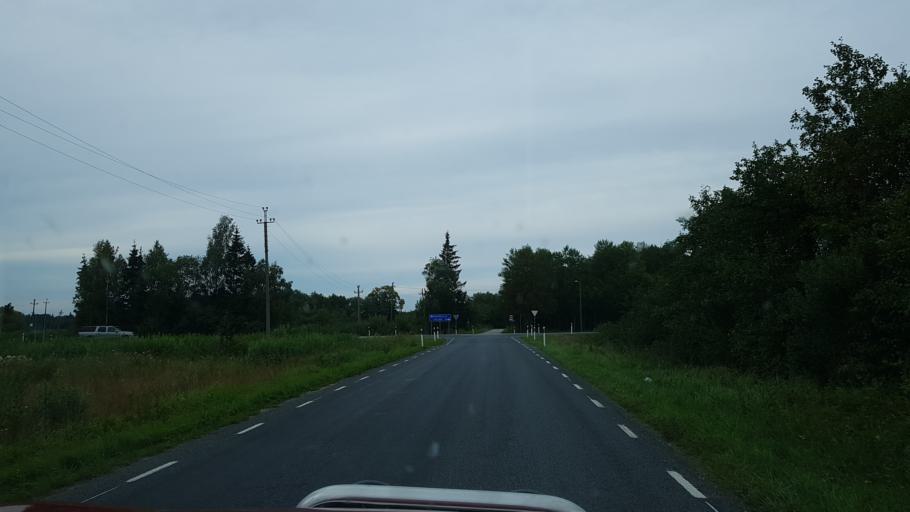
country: EE
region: Laeaene
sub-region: Ridala Parish
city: Uuemoisa
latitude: 58.9545
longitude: 23.7595
